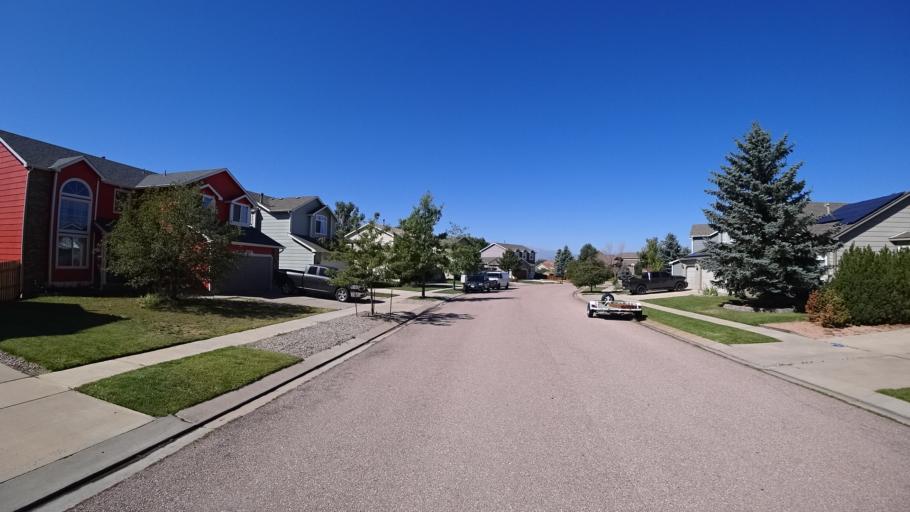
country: US
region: Colorado
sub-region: El Paso County
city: Black Forest
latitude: 38.9503
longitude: -104.7234
